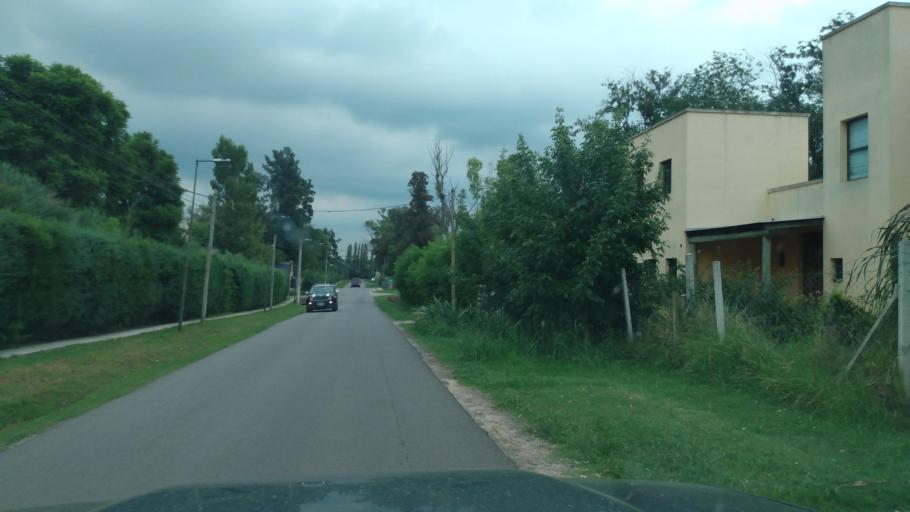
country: AR
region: Buenos Aires
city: Hurlingham
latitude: -34.5739
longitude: -58.6988
